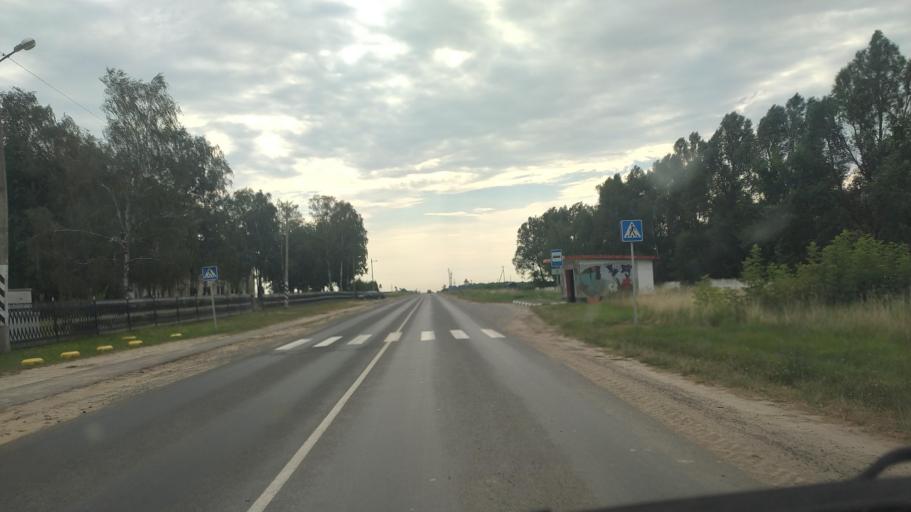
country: BY
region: Brest
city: Byaroza
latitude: 52.5515
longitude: 24.9361
